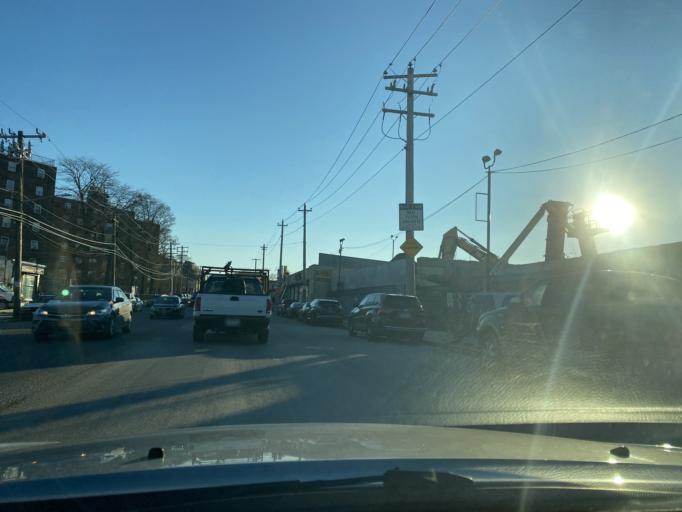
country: US
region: New York
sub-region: Nassau County
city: Inwood
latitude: 40.6112
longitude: -73.7534
